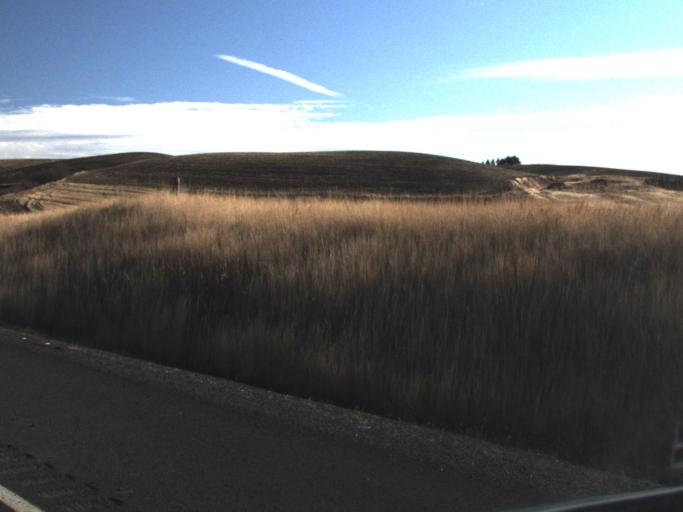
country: US
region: Washington
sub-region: Whitman County
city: Pullman
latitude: 46.7282
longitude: -117.1028
